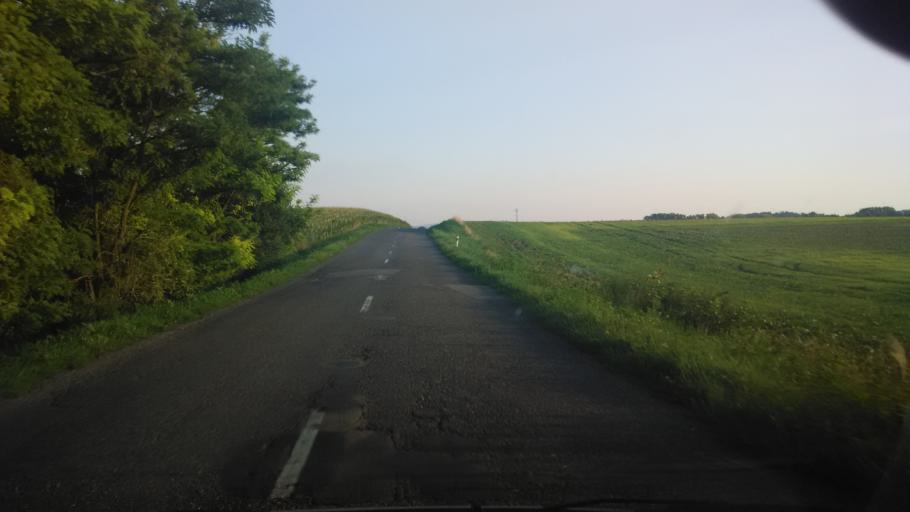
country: SK
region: Nitriansky
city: Zeliezovce
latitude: 48.0347
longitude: 18.8027
